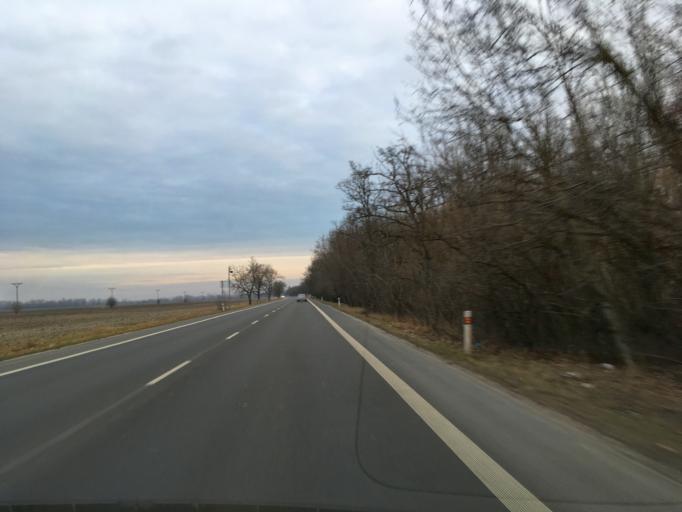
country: SK
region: Trnavsky
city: Dunajska Streda
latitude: 47.9610
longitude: 17.6952
